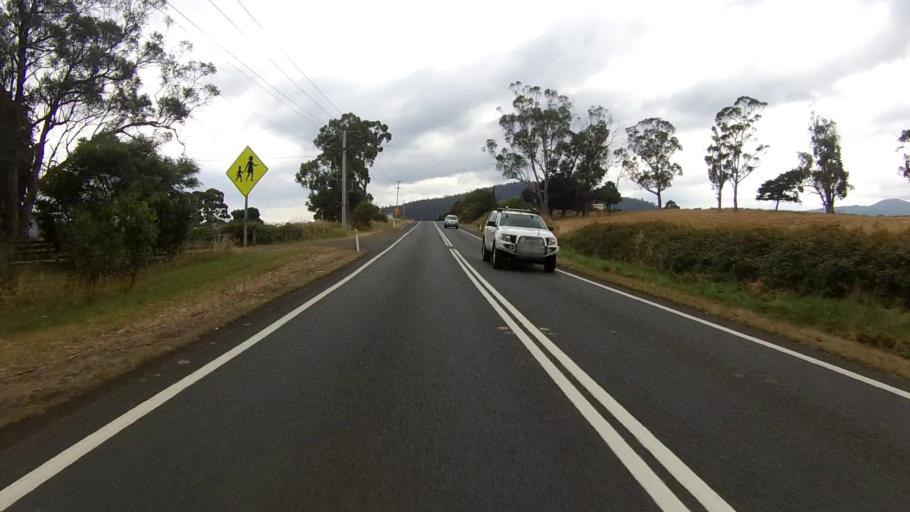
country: AU
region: Tasmania
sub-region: Huon Valley
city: Franklin
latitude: -43.0753
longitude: 147.0346
